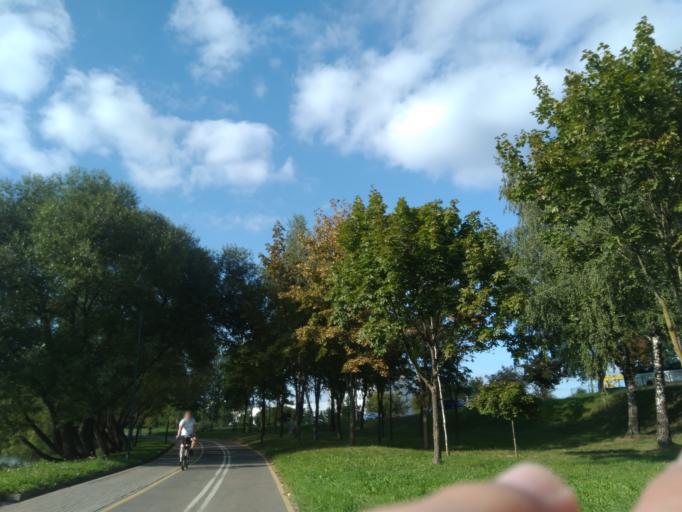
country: BY
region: Minsk
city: Minsk
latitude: 53.8744
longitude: 27.5844
